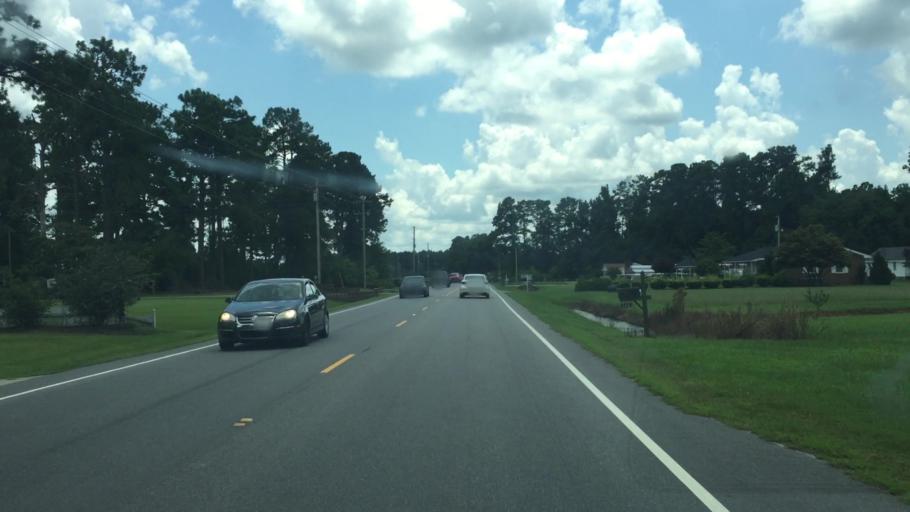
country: US
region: North Carolina
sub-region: Columbus County
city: Chadbourn
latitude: 34.2377
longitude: -78.8231
